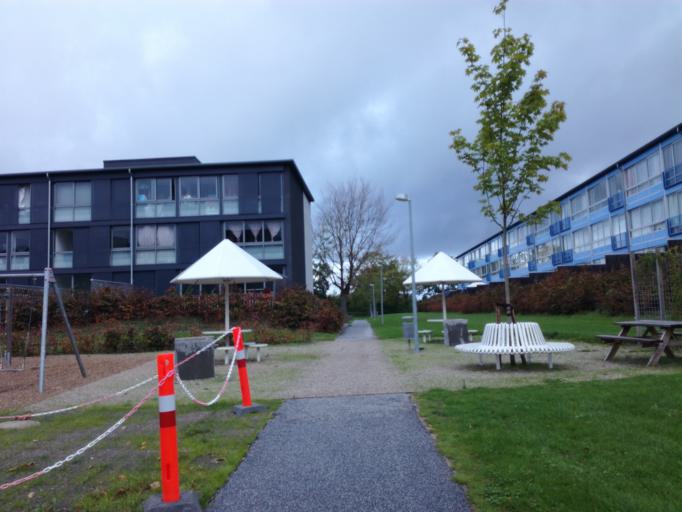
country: DK
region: South Denmark
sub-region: Fredericia Kommune
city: Fredericia
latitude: 55.5730
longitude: 9.7196
